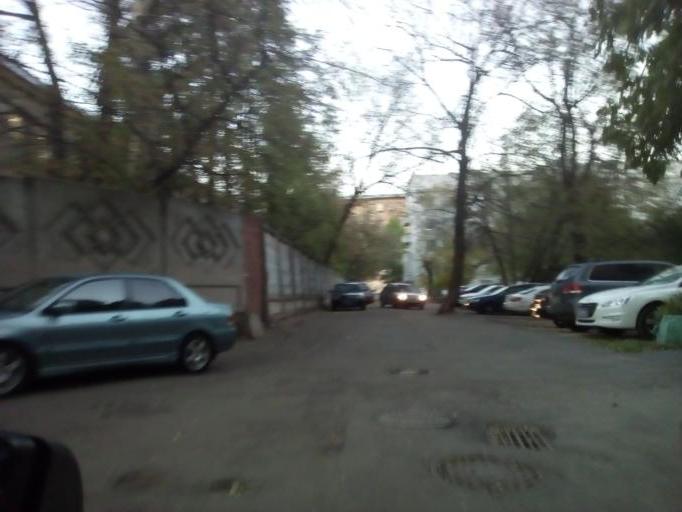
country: RU
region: Moscow
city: Sokol
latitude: 55.8065
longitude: 37.4993
